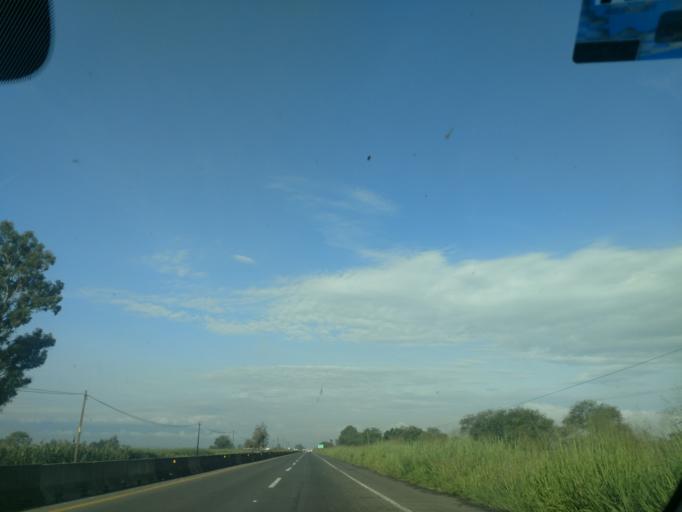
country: MX
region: Jalisco
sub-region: Ameca
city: Los Pocitos
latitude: 20.5358
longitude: -103.9502
